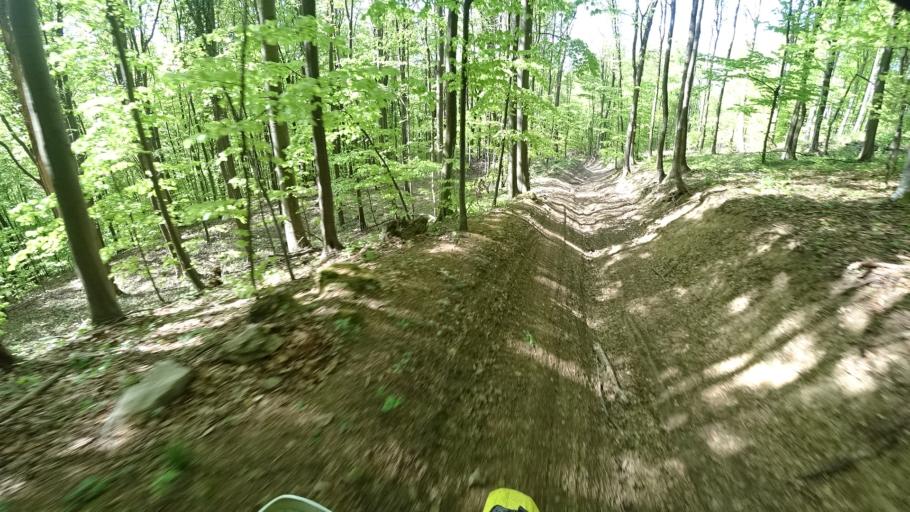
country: HR
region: Zagrebacka
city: Jablanovec
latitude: 45.8838
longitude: 15.9006
